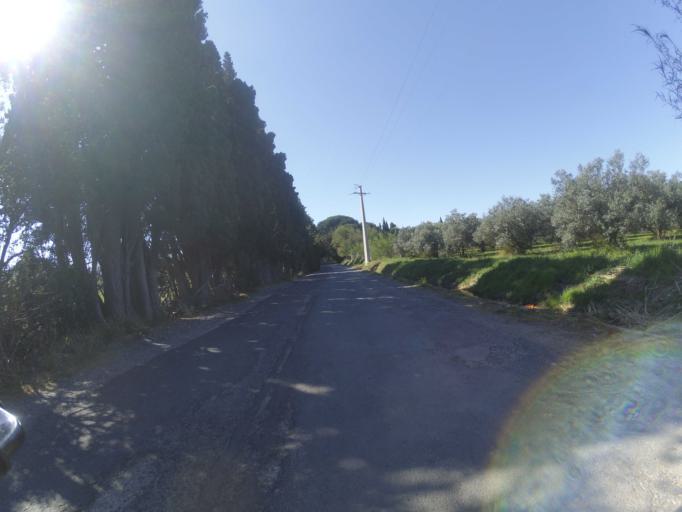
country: FR
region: Languedoc-Roussillon
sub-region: Departement des Pyrenees-Orientales
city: Pezilla-la-Riviere
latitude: 42.7012
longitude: 2.7725
